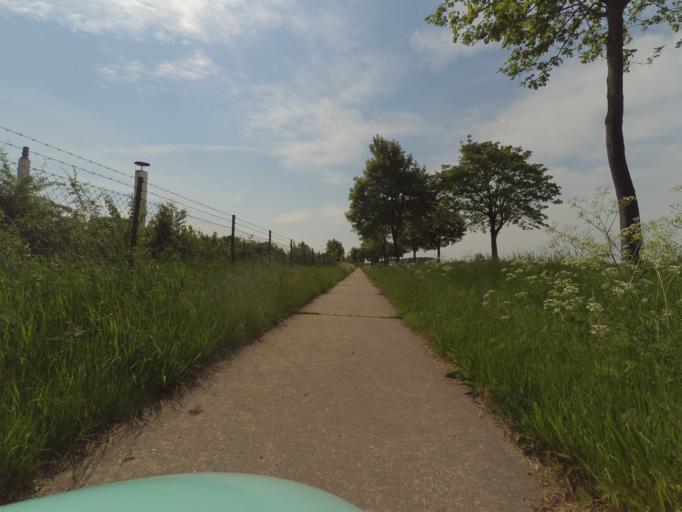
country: DE
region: Lower Saxony
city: Hohenhameln
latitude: 52.2632
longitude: 10.0516
